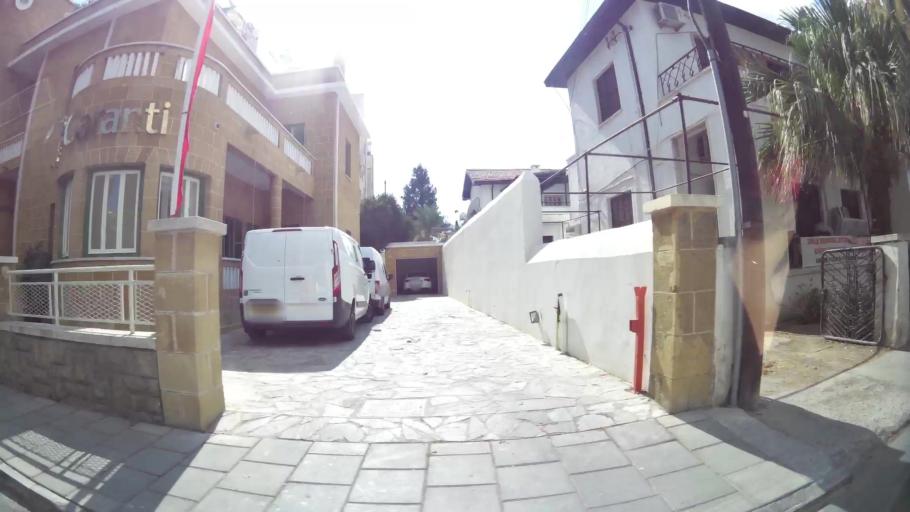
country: CY
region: Lefkosia
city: Nicosia
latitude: 35.1806
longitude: 33.3569
